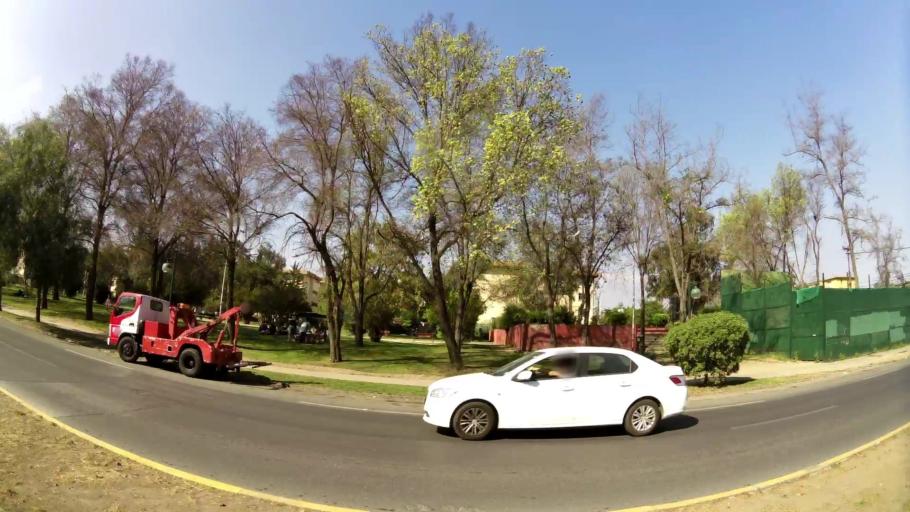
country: CL
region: Santiago Metropolitan
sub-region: Provincia de Santiago
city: Santiago
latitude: -33.4665
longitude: -70.6236
